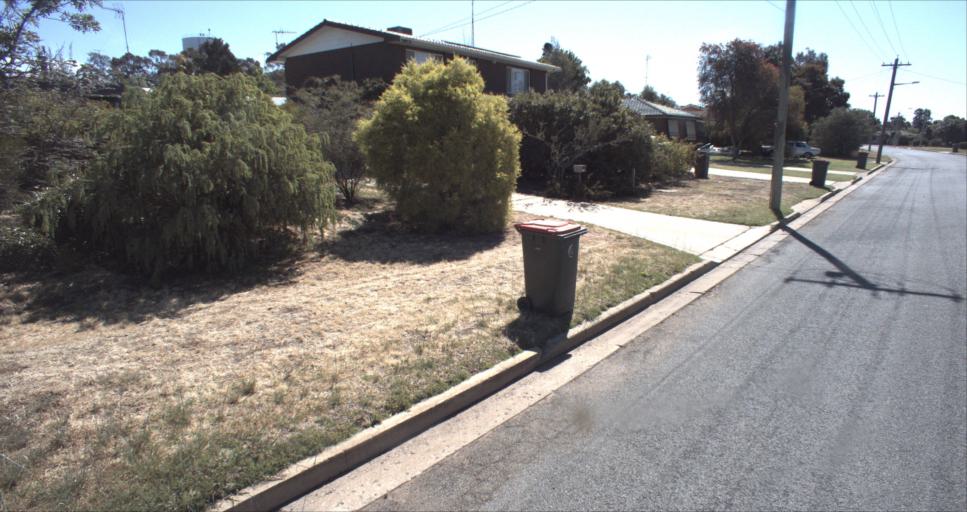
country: AU
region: New South Wales
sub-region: Leeton
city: Leeton
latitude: -34.5500
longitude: 146.3786
